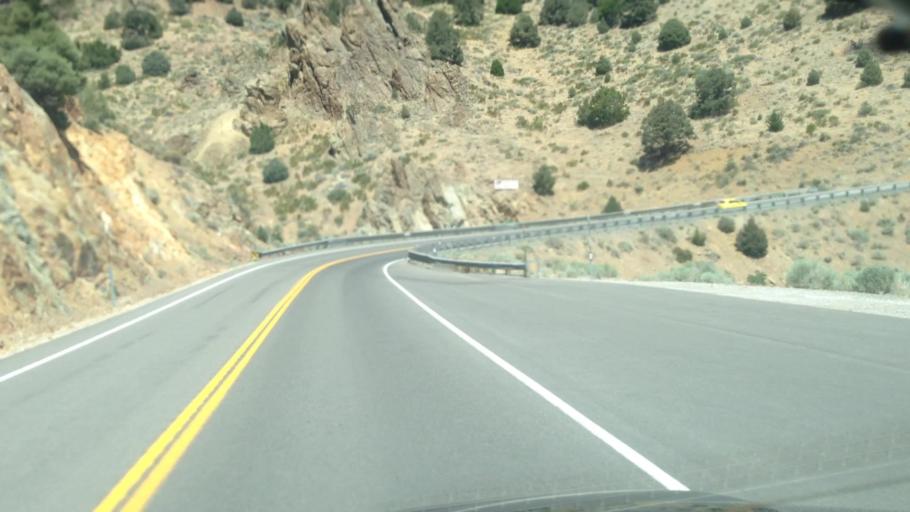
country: US
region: Nevada
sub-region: Storey County
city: Virginia City
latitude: 39.3293
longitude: -119.6457
